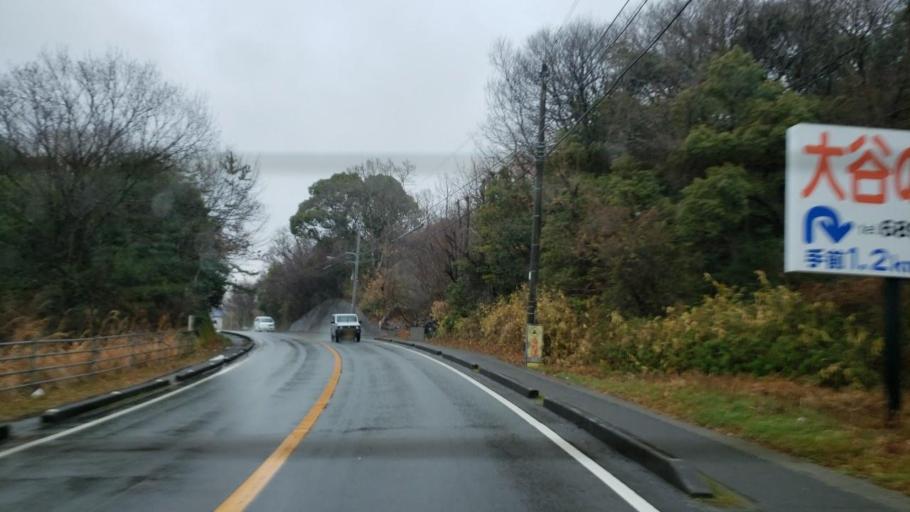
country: JP
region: Tokushima
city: Narutocho-mitsuishi
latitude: 34.1560
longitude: 134.5240
